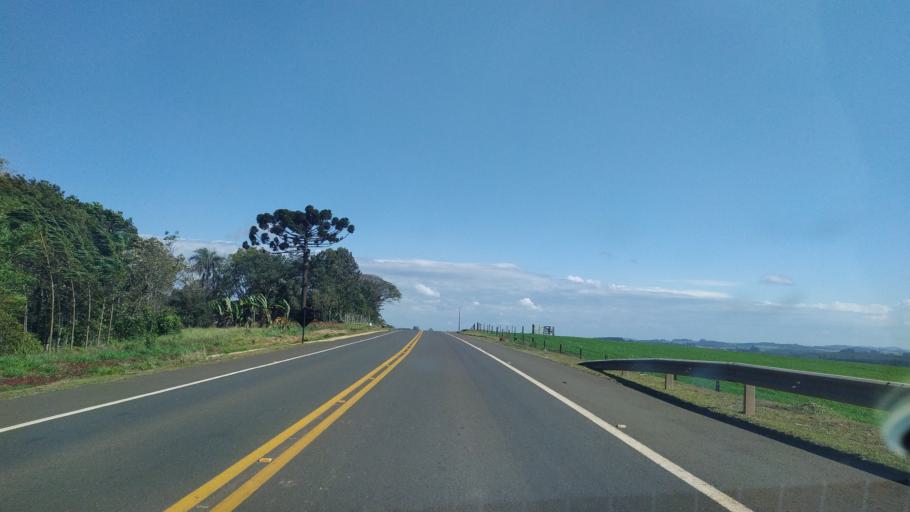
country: BR
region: Parana
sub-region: Ortigueira
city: Ortigueira
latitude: -24.2562
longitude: -50.8042
